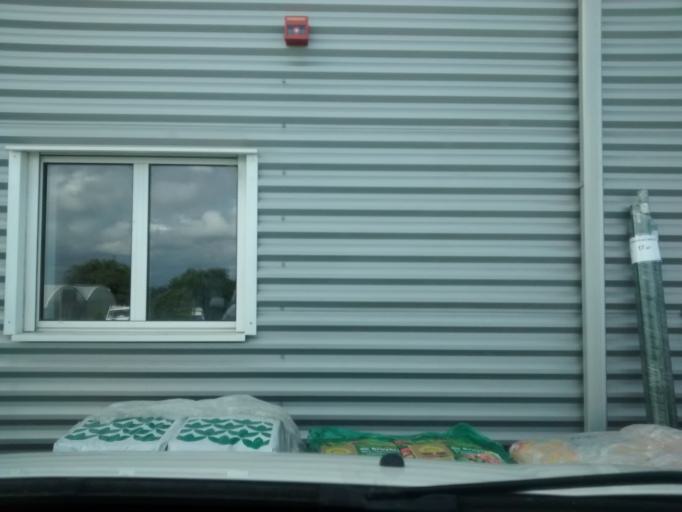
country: FR
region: Brittany
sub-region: Departement des Cotes-d'Armor
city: Penvenan
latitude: 48.7943
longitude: -3.2871
